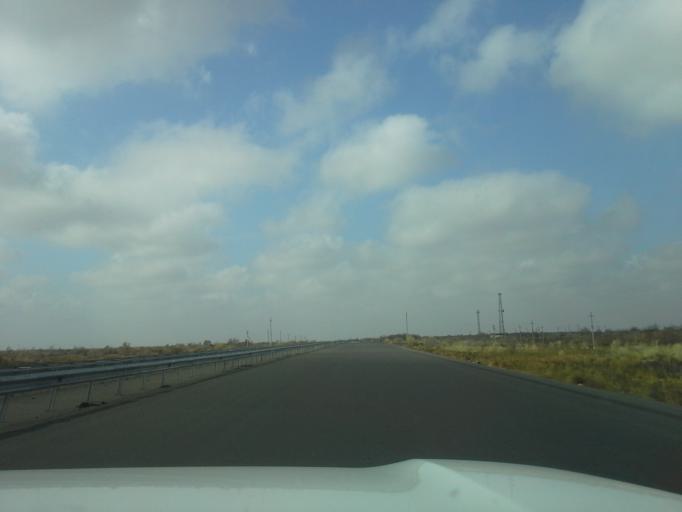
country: TM
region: Mary
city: Mary
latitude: 37.4159
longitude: 61.5554
